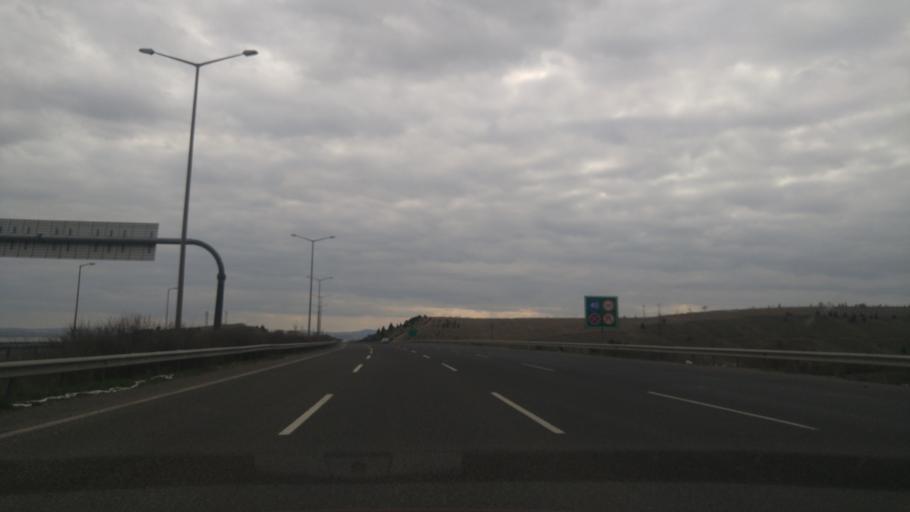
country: TR
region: Ankara
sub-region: Goelbasi
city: Golbasi
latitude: 39.8051
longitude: 32.7943
